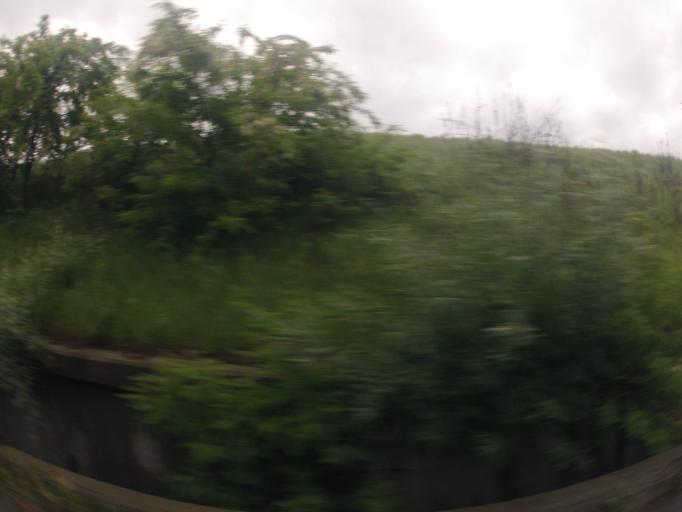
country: IT
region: Piedmont
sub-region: Provincia di Torino
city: La Loggia
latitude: 44.9495
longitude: 7.6792
